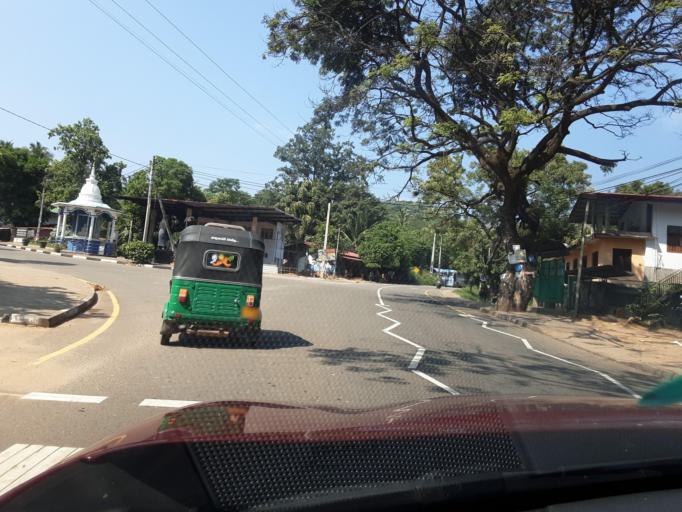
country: LK
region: Uva
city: Badulla
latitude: 7.1944
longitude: 81.0225
